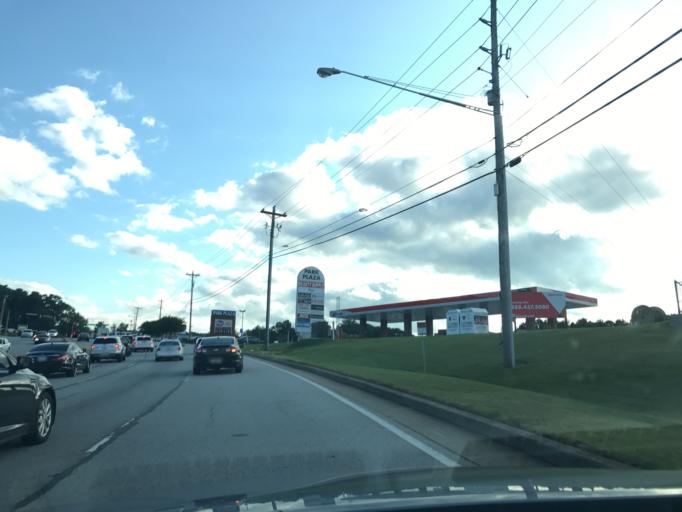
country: US
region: Georgia
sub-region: Douglas County
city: Douglasville
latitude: 33.7204
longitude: -84.7643
